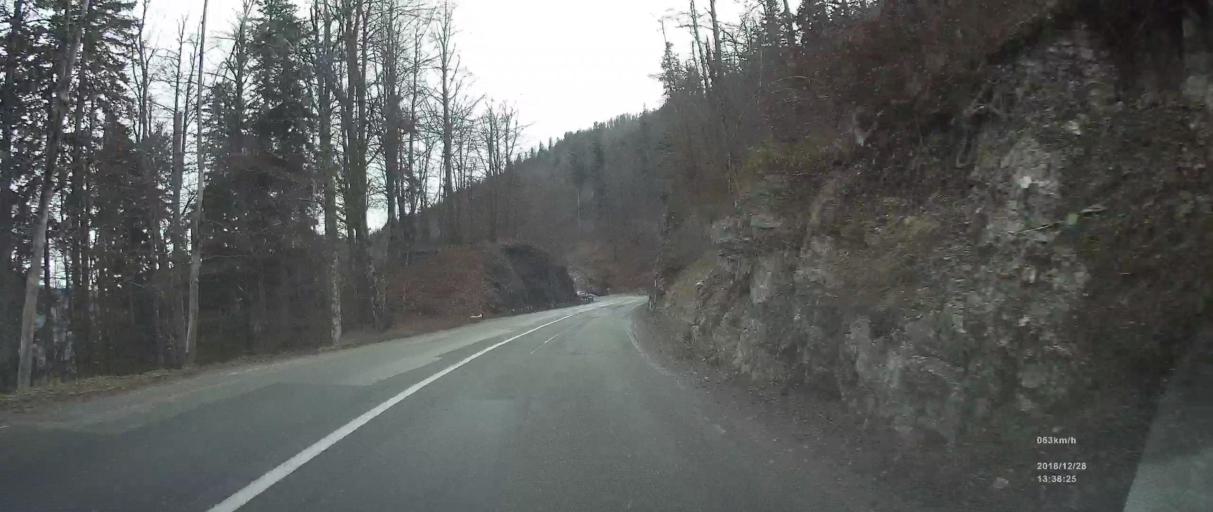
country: HR
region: Primorsko-Goranska
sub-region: Grad Delnice
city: Delnice
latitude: 45.3559
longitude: 14.7247
